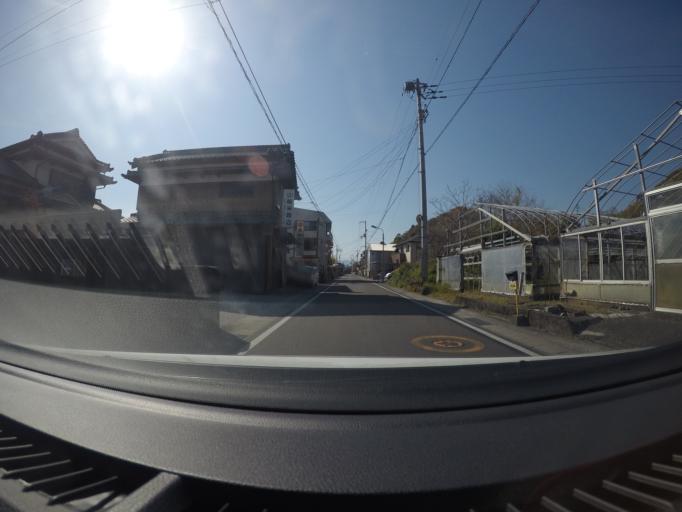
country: JP
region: Kochi
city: Kochi-shi
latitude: 33.5433
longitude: 133.5729
